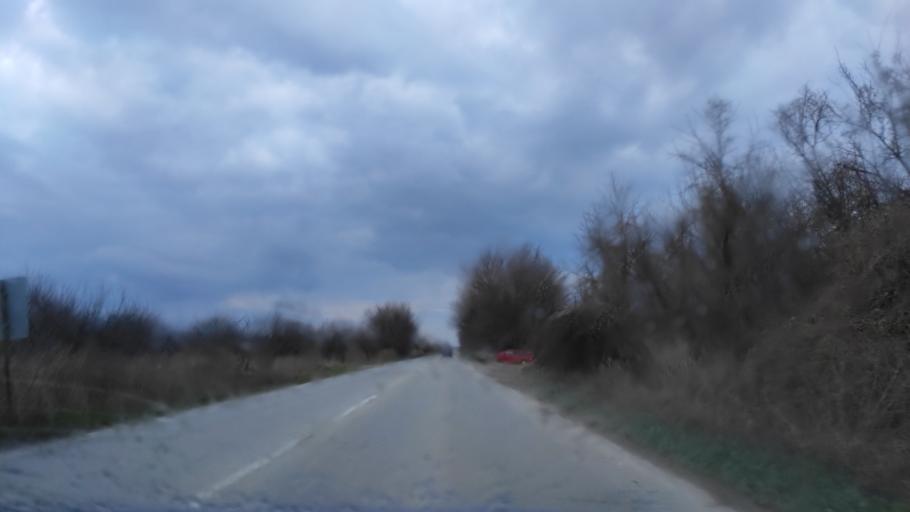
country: BG
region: Varna
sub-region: Obshtina Aksakovo
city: Aksakovo
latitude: 43.2293
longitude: 27.8267
